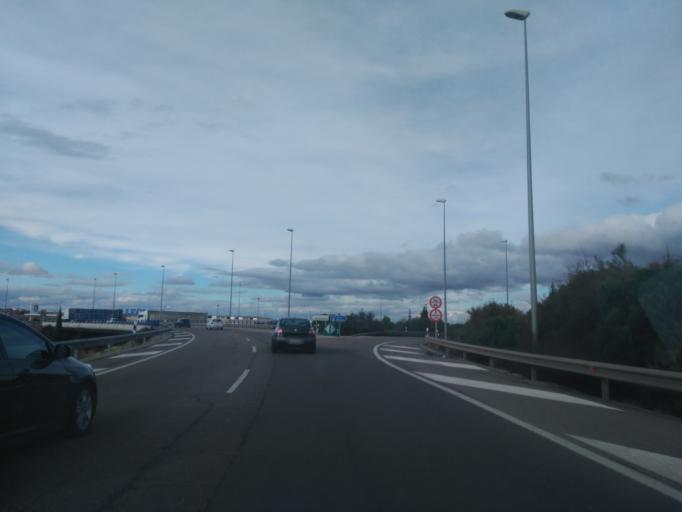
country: ES
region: Castille and Leon
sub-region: Provincia de Salamanca
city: Santa Marta de Tormes
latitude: 40.9428
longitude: -5.6387
